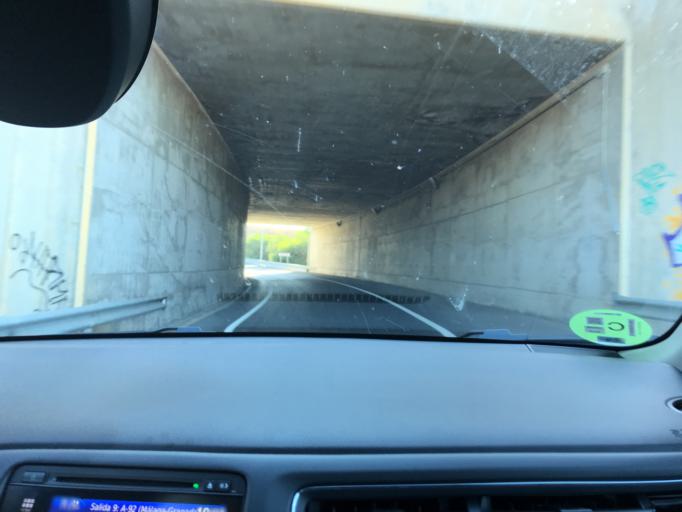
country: ES
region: Andalusia
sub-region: Provincia de Sevilla
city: Alcala de Guadaira
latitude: 37.4333
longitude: -5.8437
